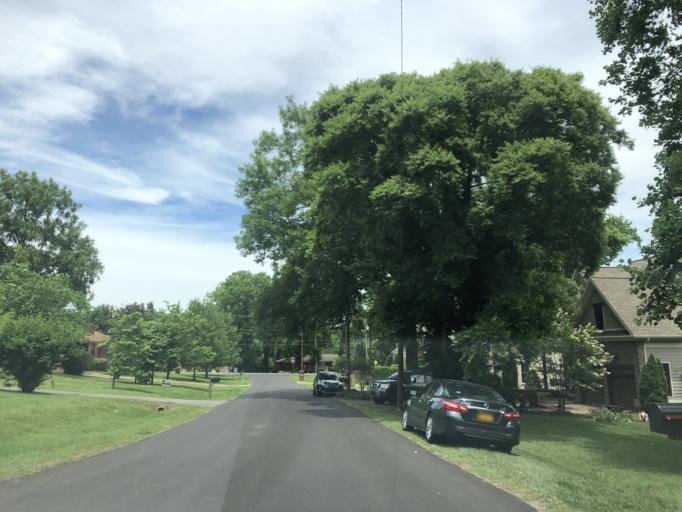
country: US
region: Tennessee
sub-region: Davidson County
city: Oak Hill
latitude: 36.1047
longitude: -86.7876
